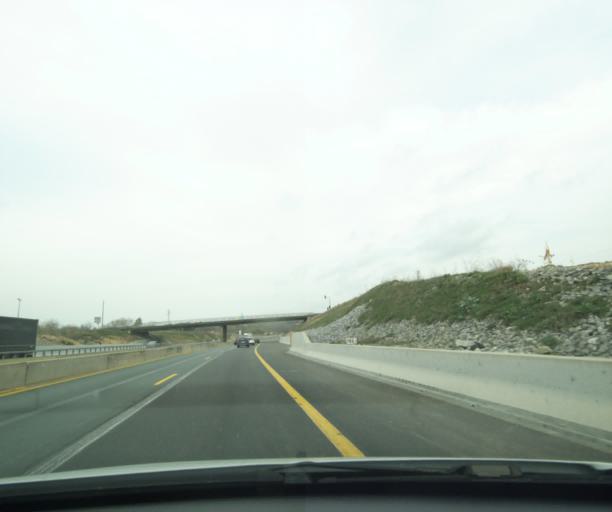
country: FR
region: Aquitaine
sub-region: Departement des Pyrenees-Atlantiques
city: Saint-Jean-de-Luz
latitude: 43.4002
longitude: -1.6357
